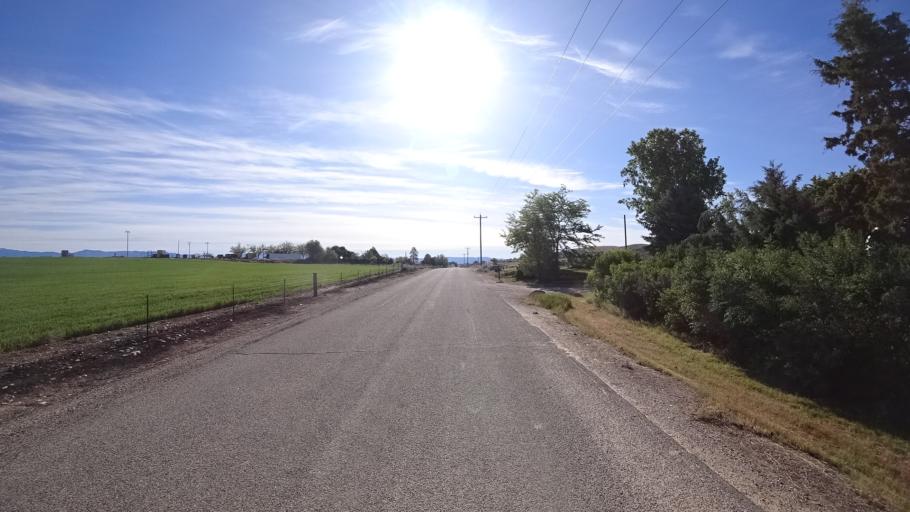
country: US
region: Idaho
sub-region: Ada County
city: Garden City
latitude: 43.5247
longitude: -116.2842
